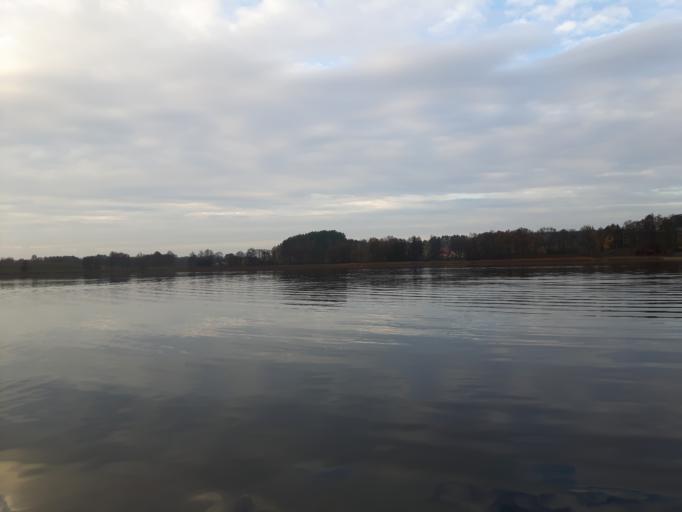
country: PL
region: Warmian-Masurian Voivodeship
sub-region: Powiat olsztynski
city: Barczewo
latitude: 53.8257
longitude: 20.7392
